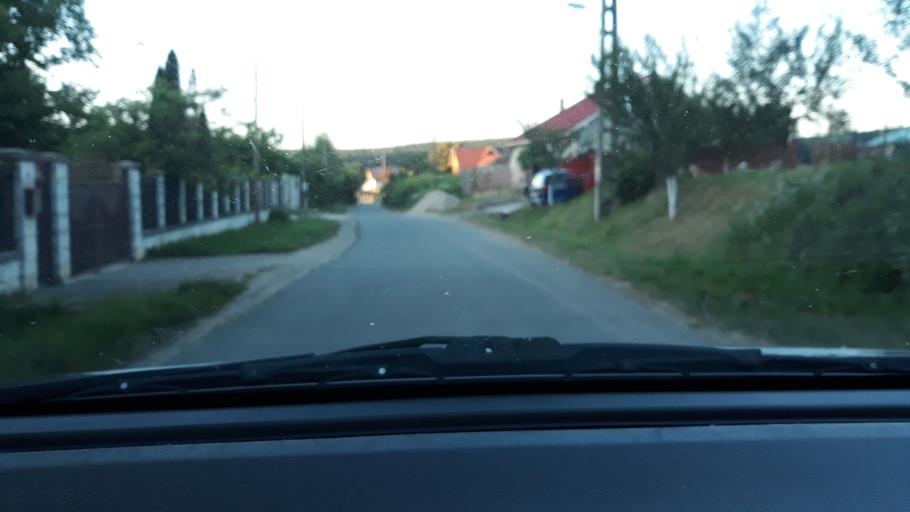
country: RO
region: Bihor
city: Hidiselu de Sus
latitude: 46.9432
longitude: 22.0211
